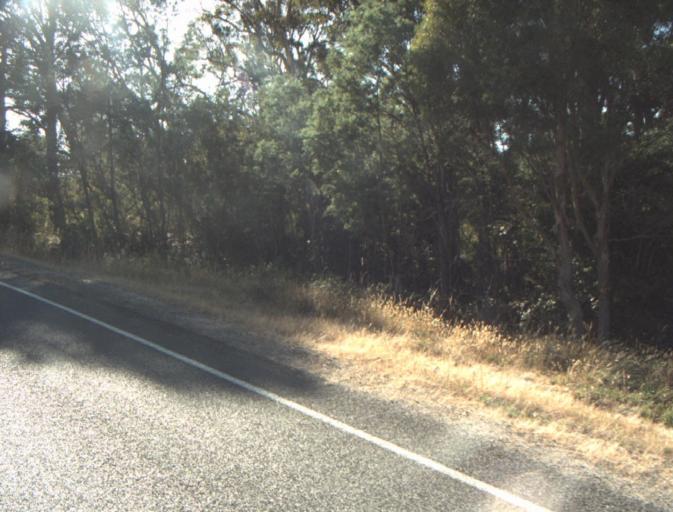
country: AU
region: Tasmania
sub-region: Launceston
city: Newstead
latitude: -41.4189
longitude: 147.2781
